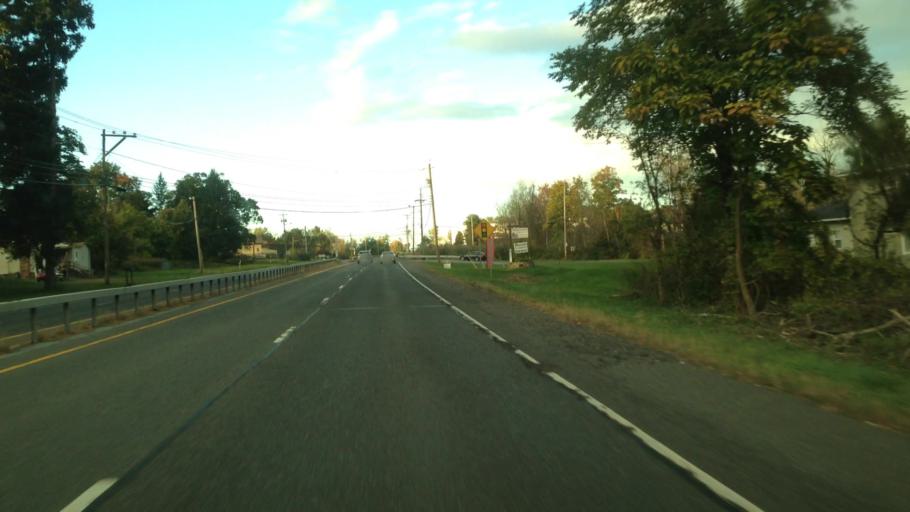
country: US
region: New York
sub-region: Ulster County
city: Highland
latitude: 41.7484
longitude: -73.9645
